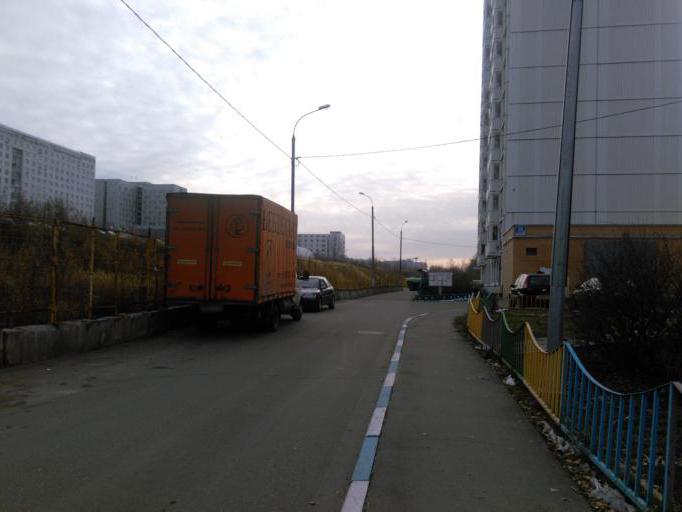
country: RU
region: Moscow
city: Troparevo
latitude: 55.6543
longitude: 37.5148
